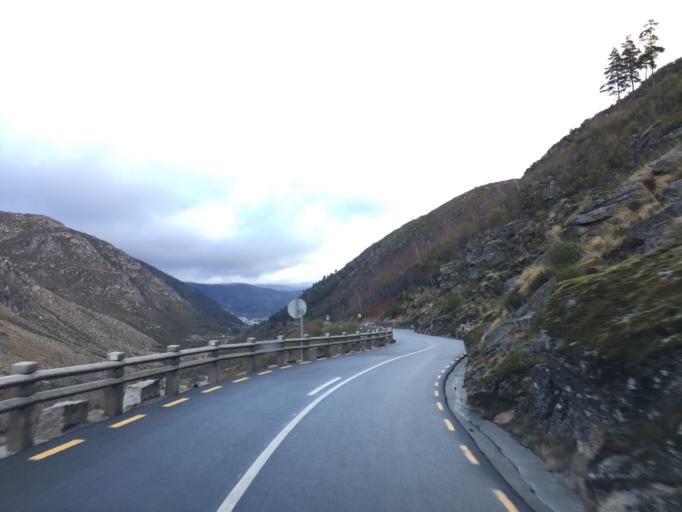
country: PT
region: Guarda
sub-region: Manteigas
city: Manteigas
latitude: 40.3405
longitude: -7.5656
